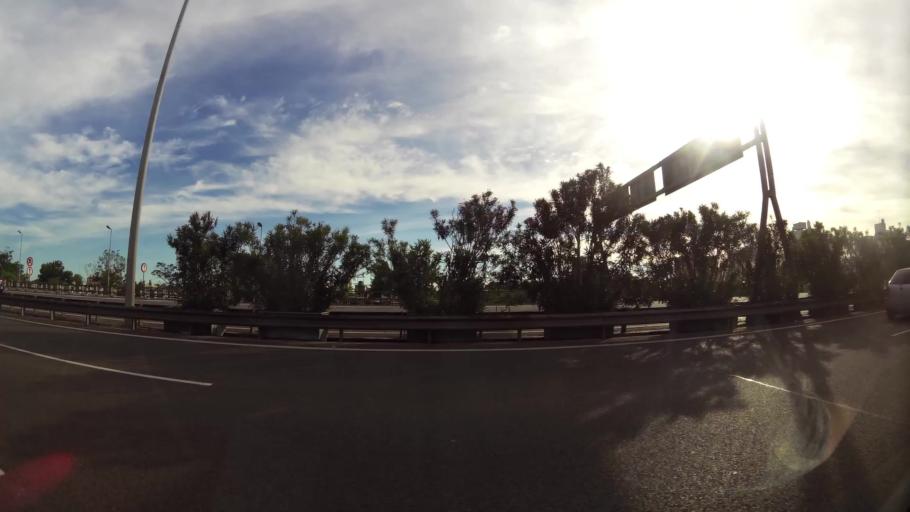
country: AR
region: Buenos Aires F.D.
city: Villa Santa Rita
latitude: -34.6436
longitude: -58.4891
